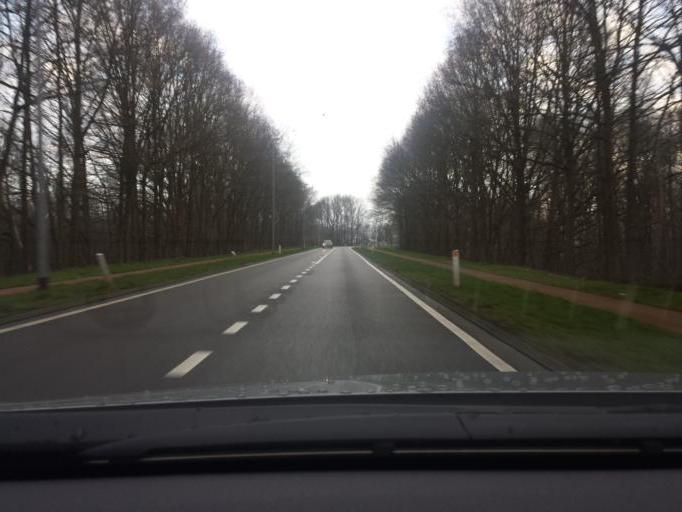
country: BE
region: Flanders
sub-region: Provincie Limburg
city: Lummen
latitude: 51.0207
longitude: 5.2048
